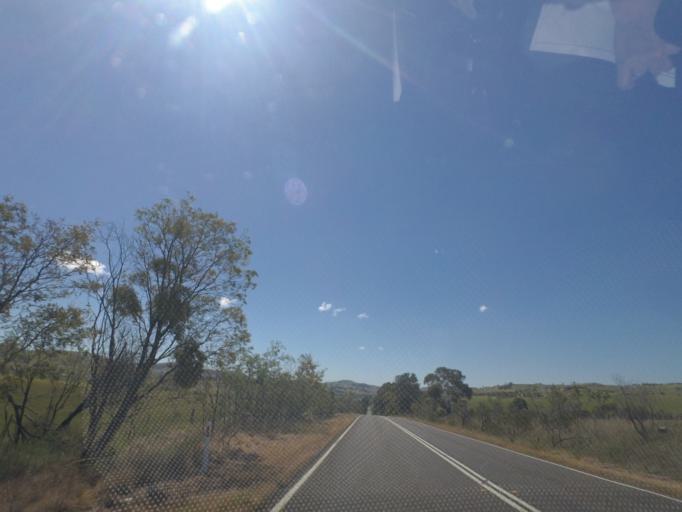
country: AU
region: Victoria
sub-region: Hume
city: Sunbury
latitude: -37.1151
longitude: 144.7595
